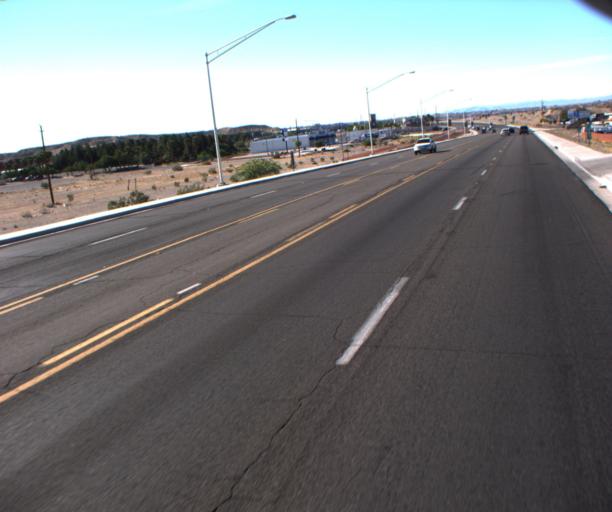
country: US
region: Arizona
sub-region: Mohave County
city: Bullhead City
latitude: 35.0877
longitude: -114.5980
